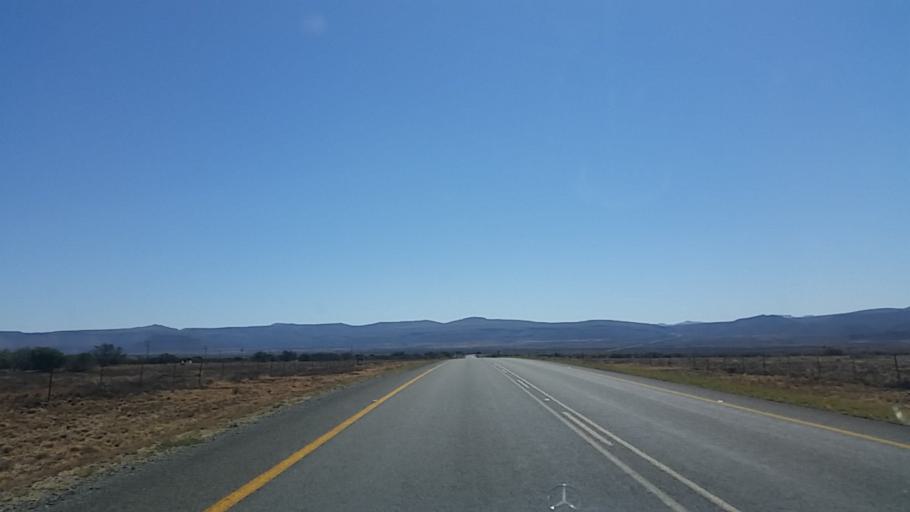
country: ZA
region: Eastern Cape
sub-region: Cacadu District Municipality
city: Graaff-Reinet
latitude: -32.0381
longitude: 24.6206
